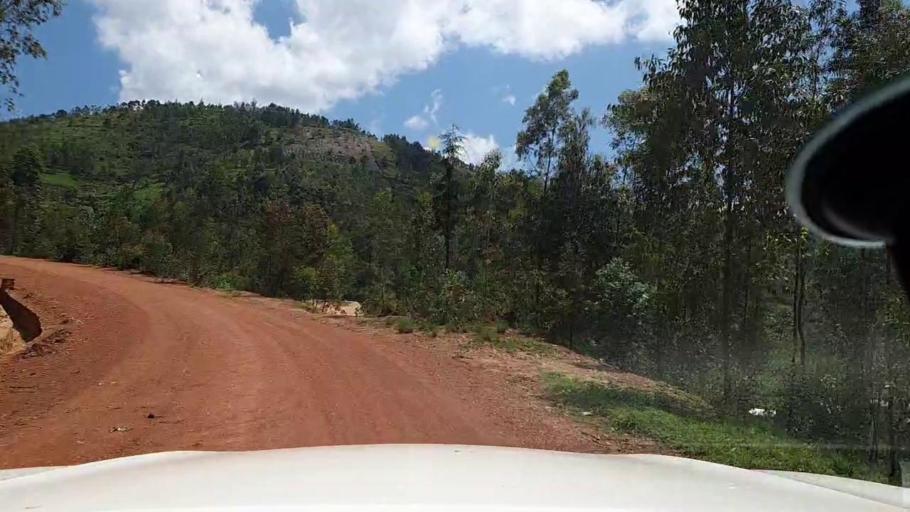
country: RW
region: Northern Province
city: Byumba
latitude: -1.7396
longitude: 29.8615
